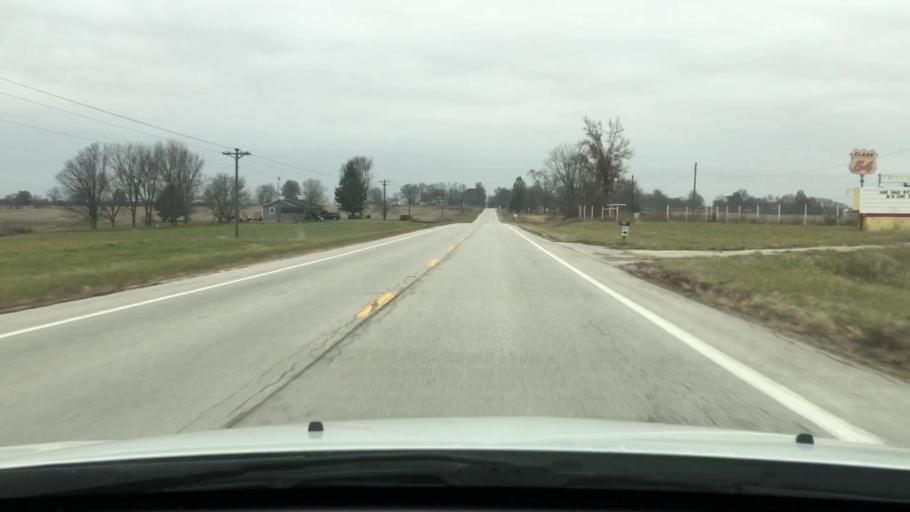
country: US
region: Illinois
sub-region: Pike County
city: Pittsfield
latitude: 39.5360
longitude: -90.9206
